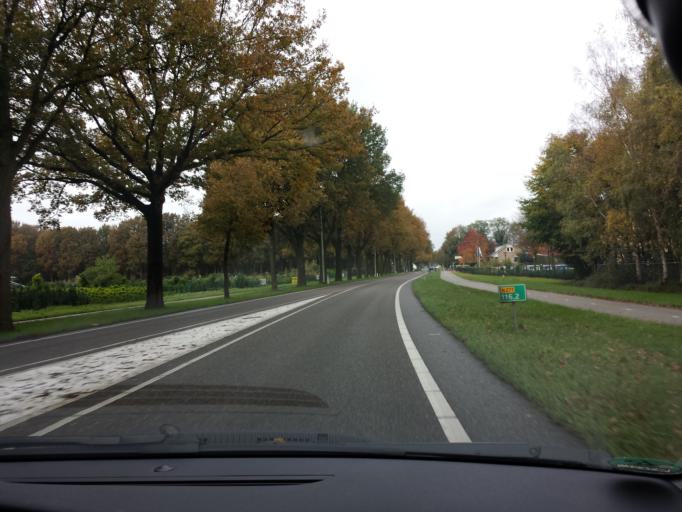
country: NL
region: Limburg
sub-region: Gemeente Gennep
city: Gennep
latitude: 51.7165
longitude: 5.9587
